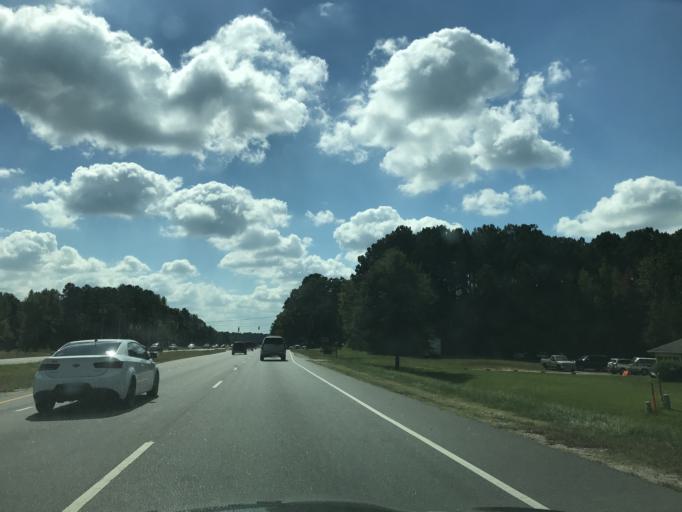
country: US
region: North Carolina
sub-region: Wake County
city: Wake Forest
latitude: 36.0065
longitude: -78.5206
